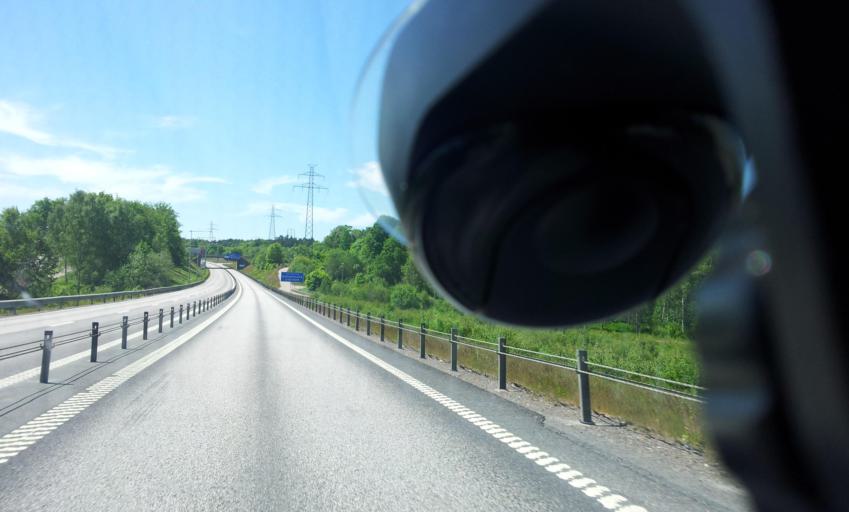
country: SE
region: Kalmar
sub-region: Oskarshamns Kommun
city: Oskarshamn
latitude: 57.2681
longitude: 16.4333
